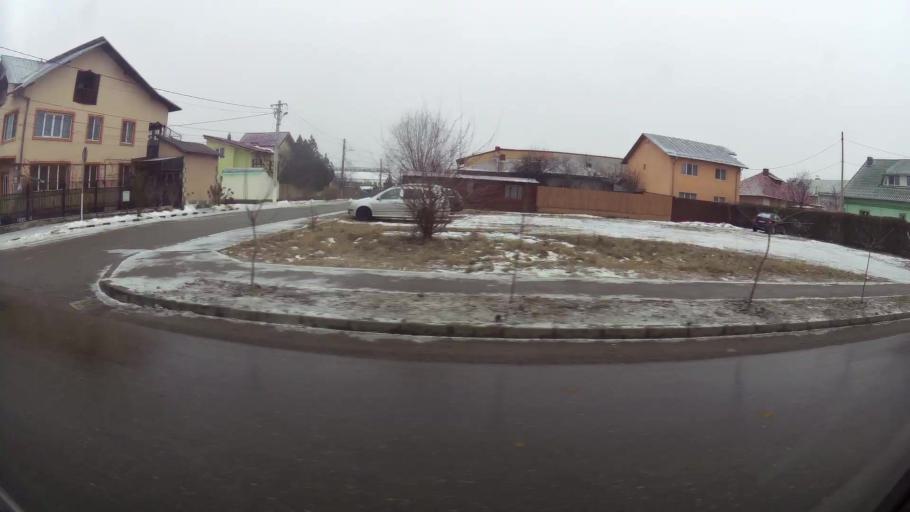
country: RO
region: Prahova
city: Ploiesti
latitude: 44.9514
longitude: 26.0462
